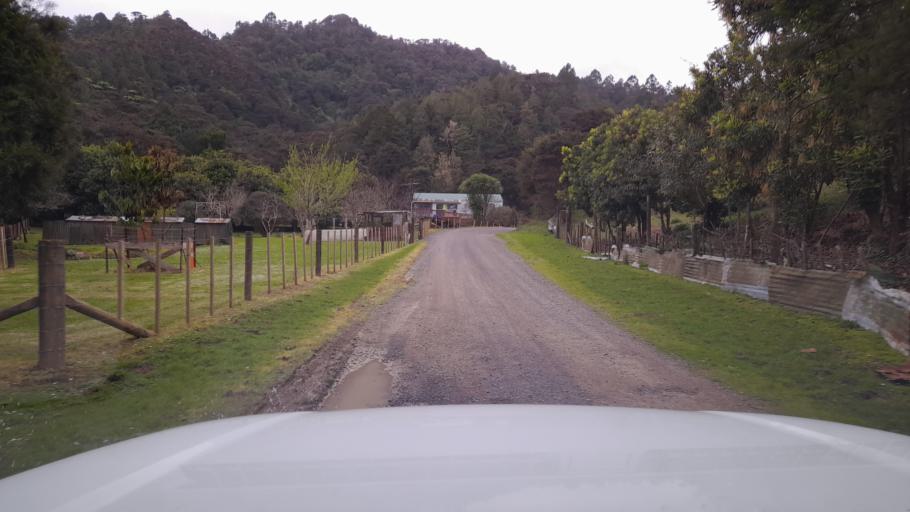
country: NZ
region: Northland
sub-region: Far North District
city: Paihia
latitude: -35.3537
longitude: 174.2348
